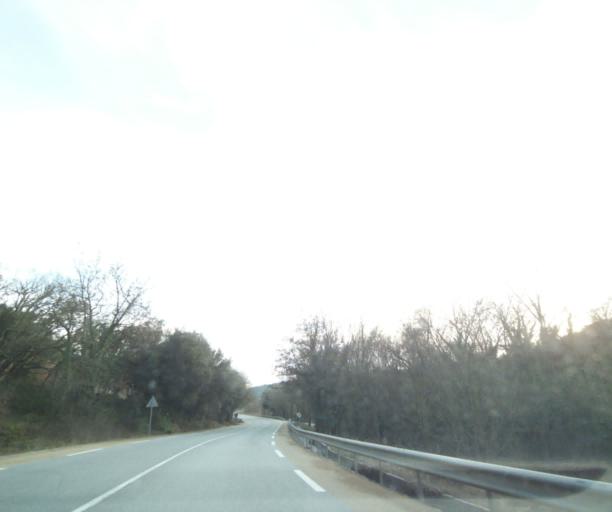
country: FR
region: Provence-Alpes-Cote d'Azur
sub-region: Departement du Var
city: Trans-en-Provence
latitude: 43.4985
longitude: 6.5101
